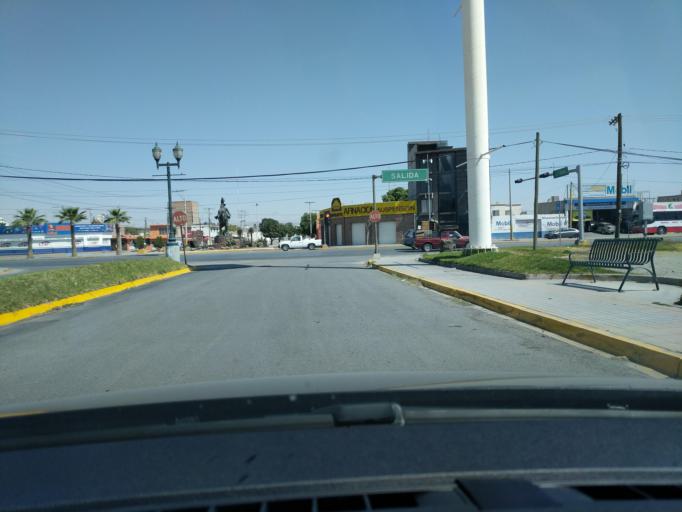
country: MX
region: Coahuila
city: Torreon
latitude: 25.5347
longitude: -103.4037
